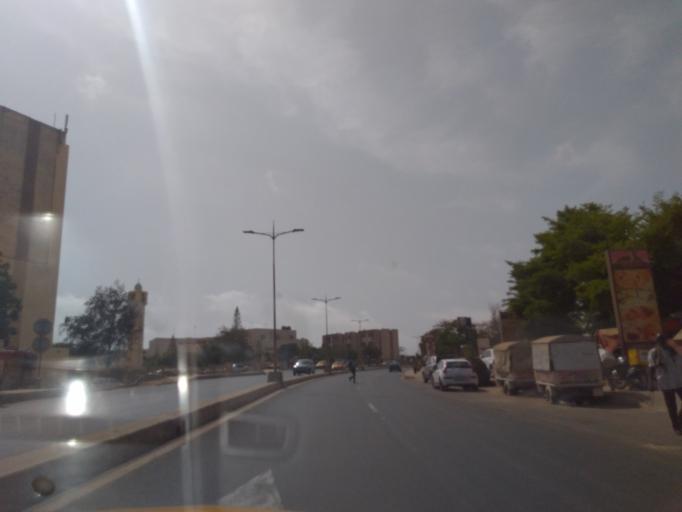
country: SN
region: Dakar
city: Mermoz Boabab
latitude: 14.7081
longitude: -17.4806
